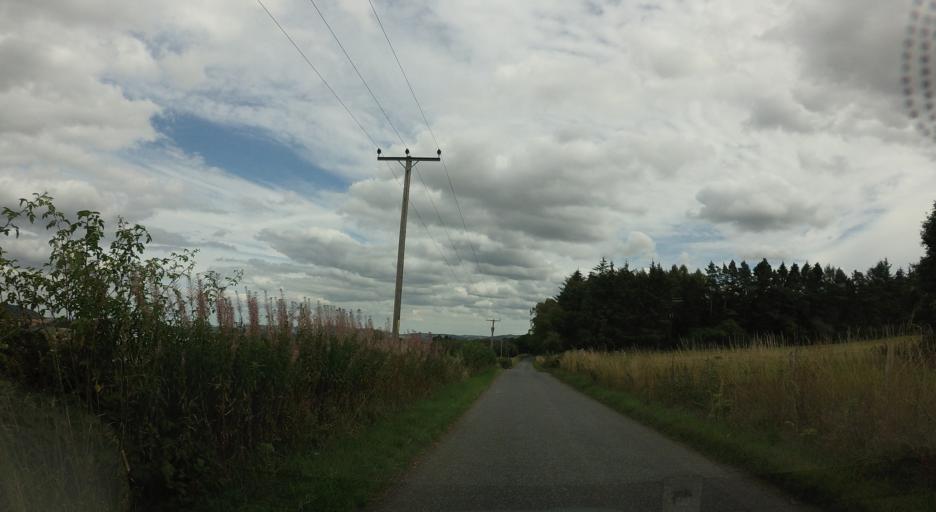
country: GB
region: Scotland
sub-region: Perth and Kinross
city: Bridge of Earn
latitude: 56.3687
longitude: -3.3769
